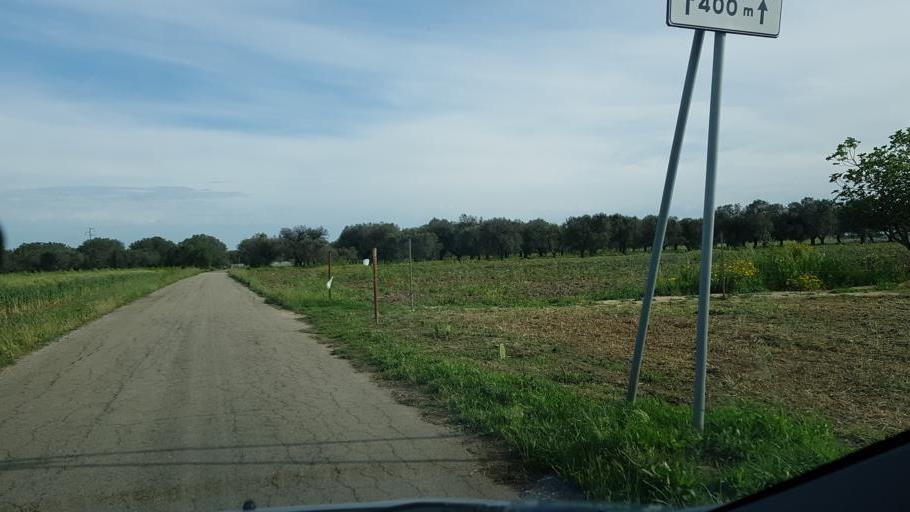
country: IT
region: Apulia
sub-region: Provincia di Brindisi
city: Tuturano
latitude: 40.5240
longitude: 17.9694
